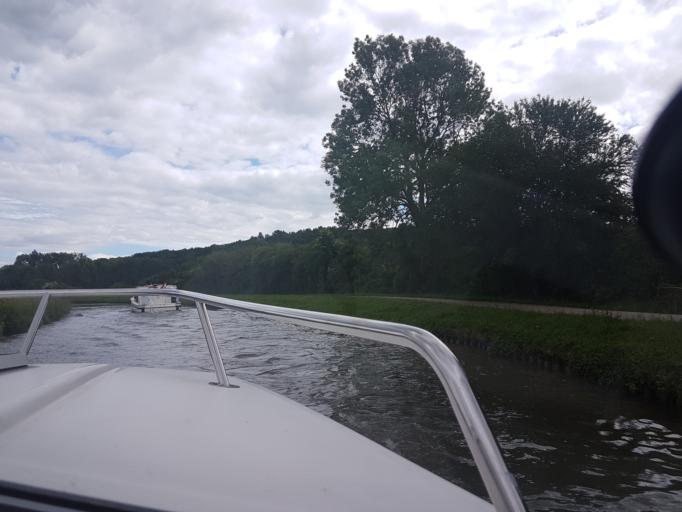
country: FR
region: Bourgogne
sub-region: Departement de l'Yonne
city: Vermenton
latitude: 47.5688
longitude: 3.6377
